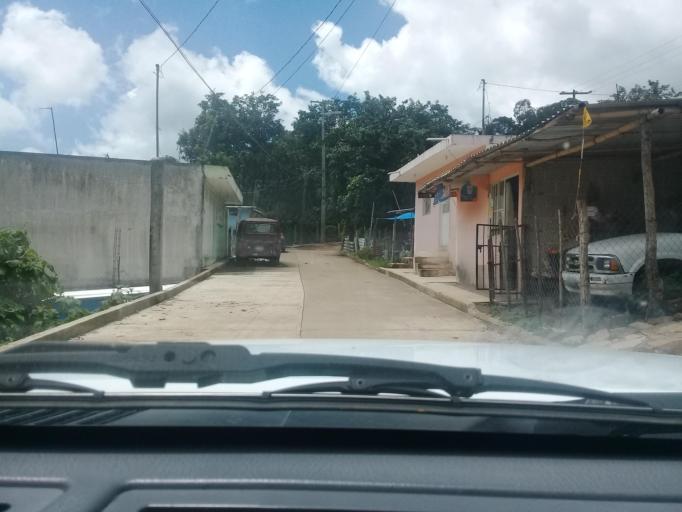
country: MX
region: Veracruz
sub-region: Tlalnelhuayocan
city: Otilpan
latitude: 19.5552
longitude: -96.9787
